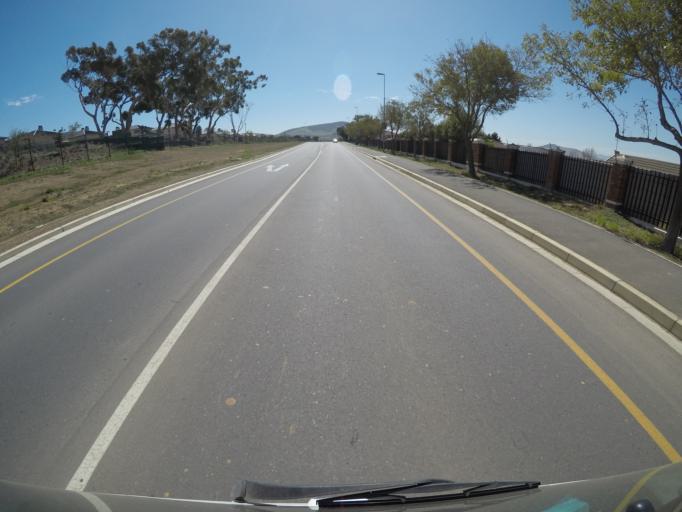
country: ZA
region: Western Cape
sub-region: City of Cape Town
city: Kraaifontein
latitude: -33.8213
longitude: 18.6359
